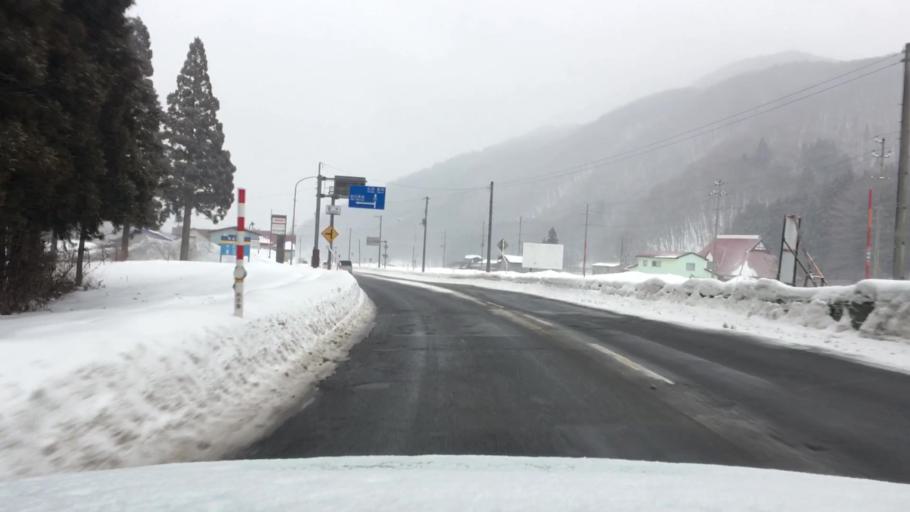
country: JP
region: Akita
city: Hanawa
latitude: 40.0335
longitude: 140.9892
